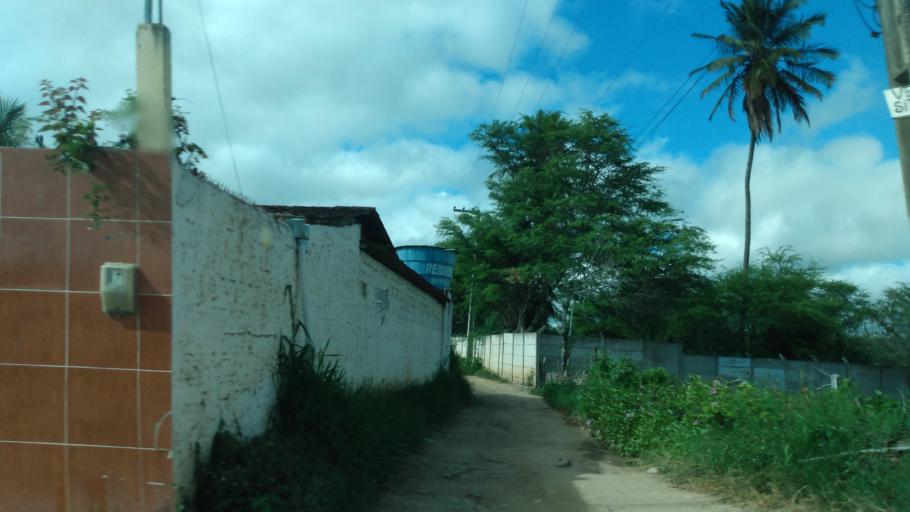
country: BR
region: Pernambuco
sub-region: Caruaru
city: Caruaru
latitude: -8.3019
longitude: -35.9998
